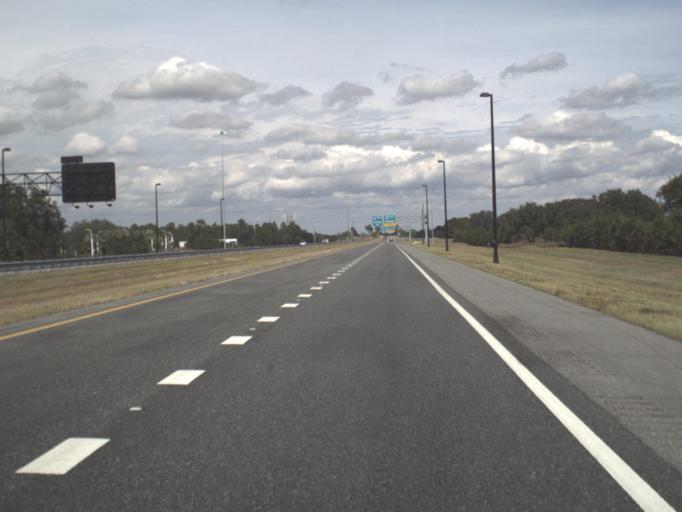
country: US
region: Florida
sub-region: Polk County
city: Polk City
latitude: 28.1458
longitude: -81.8435
